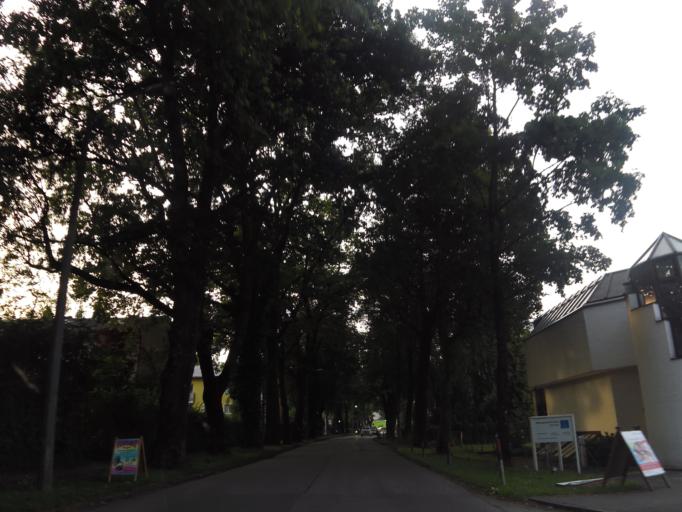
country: AT
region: Salzburg
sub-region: Salzburg Stadt
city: Salzburg
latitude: 47.7886
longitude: 13.0483
